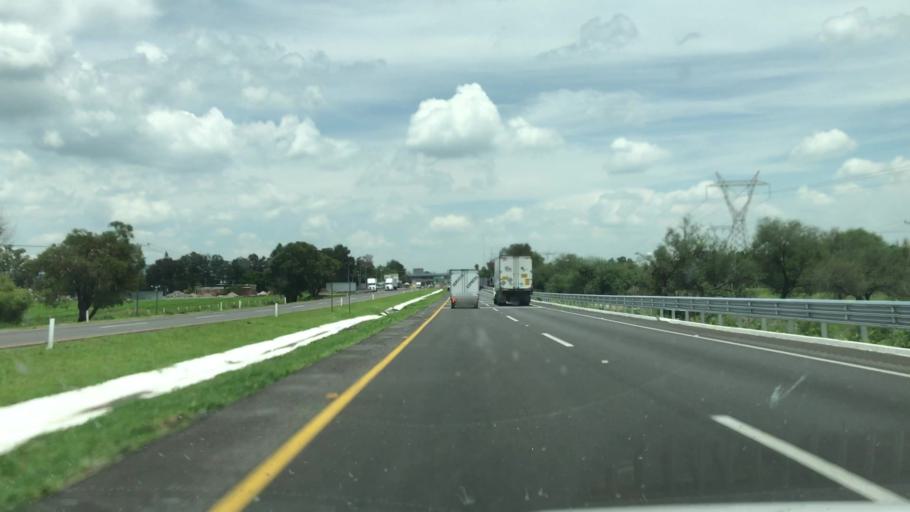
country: MX
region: Guanajuato
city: Salamanca
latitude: 20.5995
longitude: -101.1868
